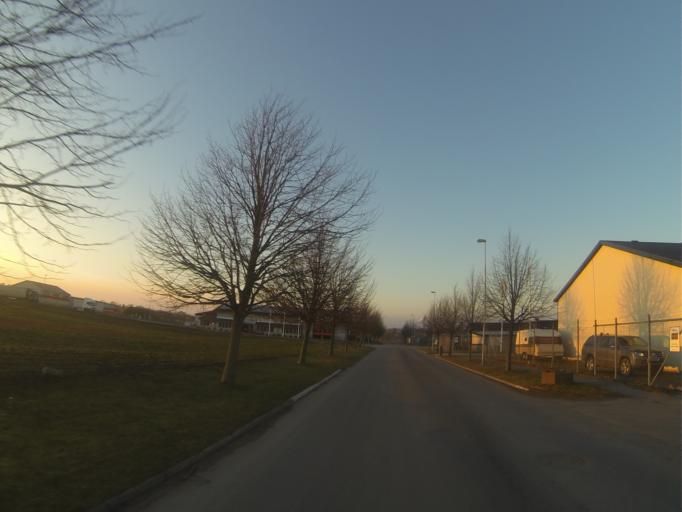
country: SE
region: Skane
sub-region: Burlovs Kommun
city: Arloev
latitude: 55.6141
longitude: 13.0958
